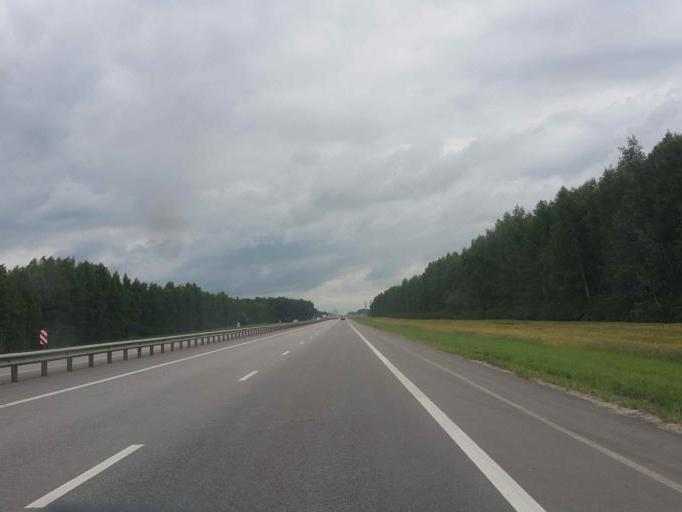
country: RU
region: Tambov
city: Zavoronezhskoye
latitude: 52.8512
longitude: 40.7967
